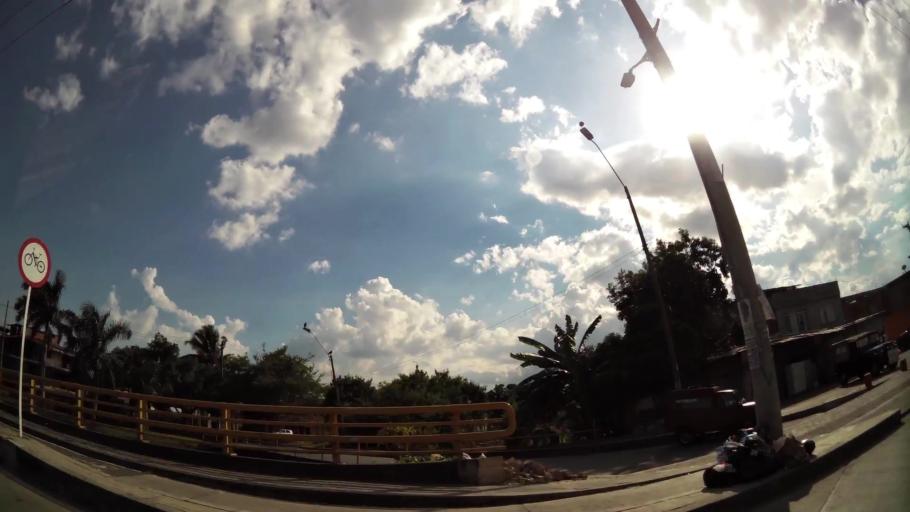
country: CO
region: Valle del Cauca
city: Cali
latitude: 3.4196
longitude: -76.4885
